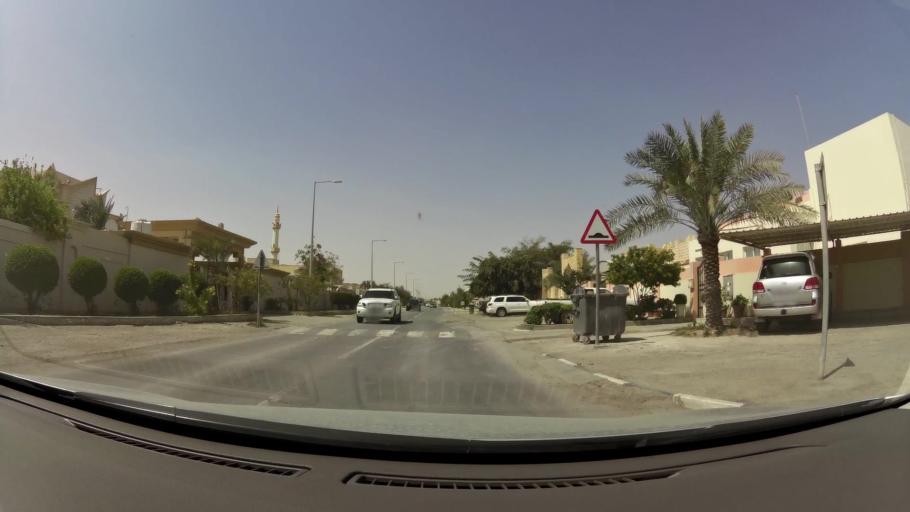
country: QA
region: Baladiyat Umm Salal
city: Umm Salal Muhammad
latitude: 25.3765
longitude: 51.4262
